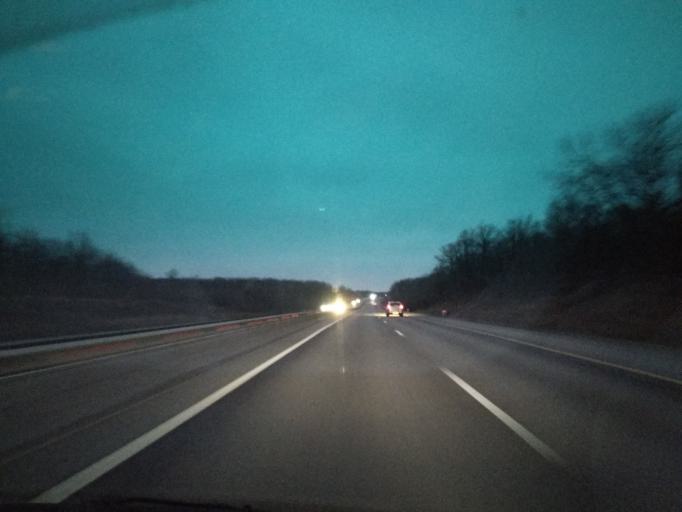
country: RU
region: Krasnodarskiy
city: Saratovskaya
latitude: 44.7470
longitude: 39.2259
